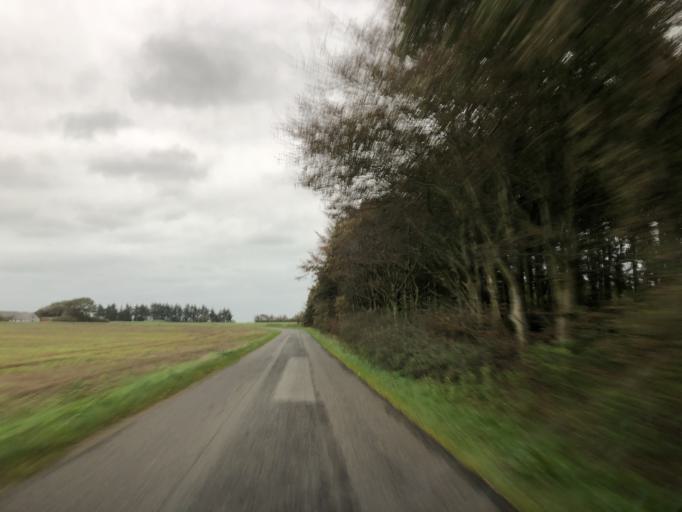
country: DK
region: Central Jutland
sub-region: Herning Kommune
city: Vildbjerg
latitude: 56.1999
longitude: 8.6676
